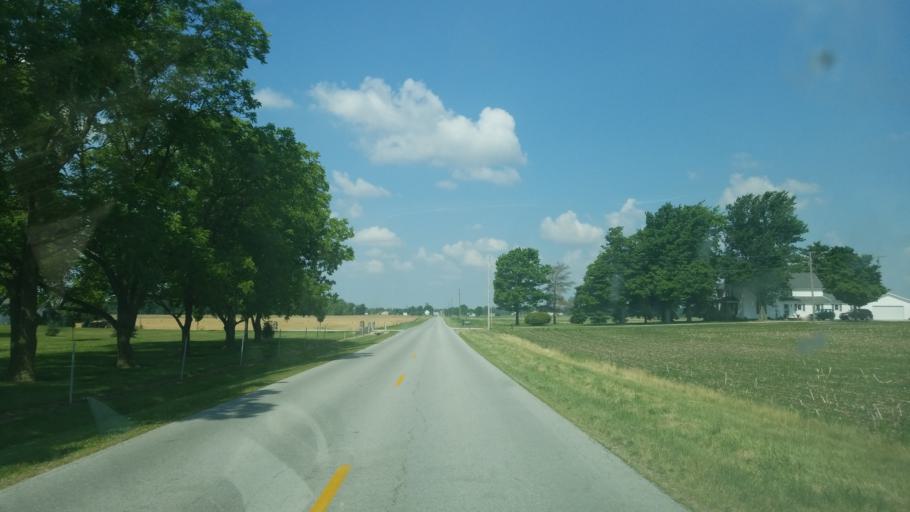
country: US
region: Ohio
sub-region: Auglaize County
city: Wapakoneta
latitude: 40.5702
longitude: -84.1482
